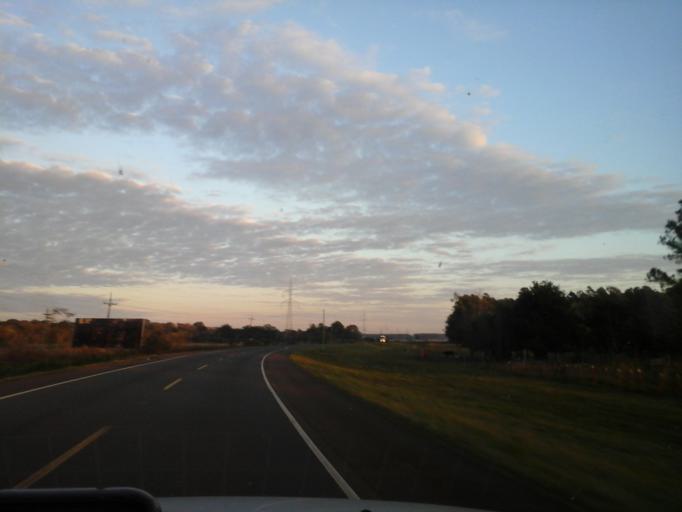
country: PY
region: Itapua
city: General Delgado
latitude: -27.0728
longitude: -56.6026
